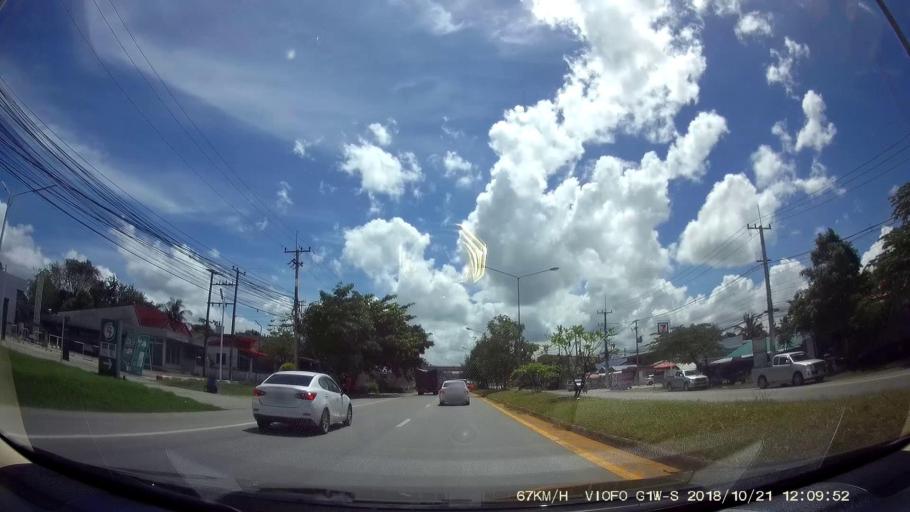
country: TH
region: Chaiyaphum
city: Chatturat
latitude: 15.4162
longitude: 101.8333
